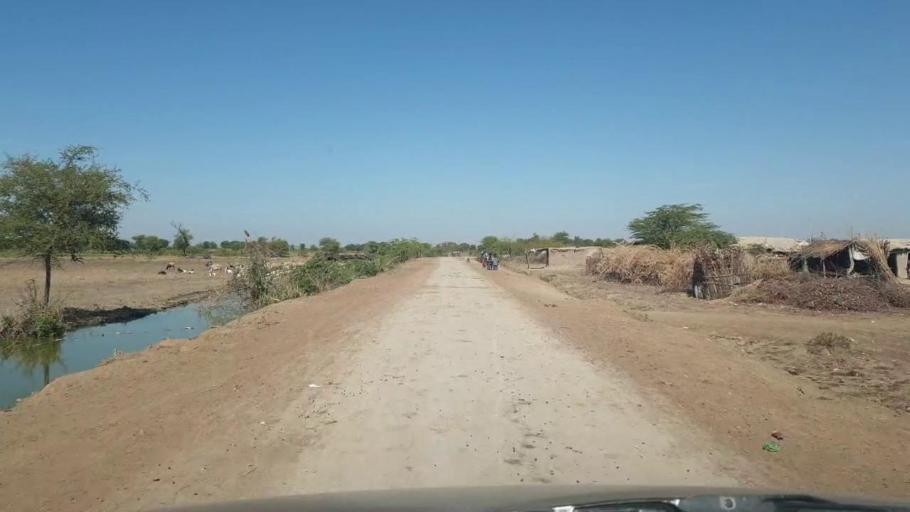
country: PK
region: Sindh
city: Umarkot
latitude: 25.4203
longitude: 69.6448
